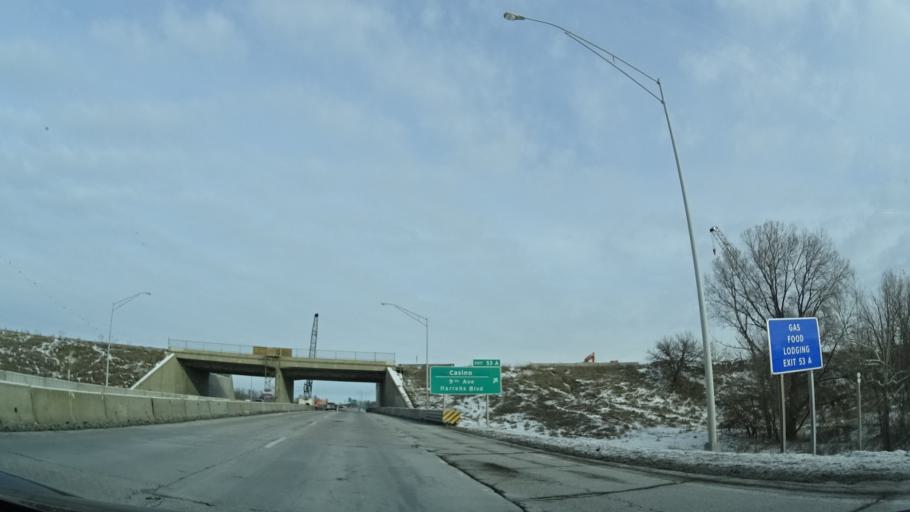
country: US
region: Nebraska
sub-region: Douglas County
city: Omaha
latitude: 41.2487
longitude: -95.9067
